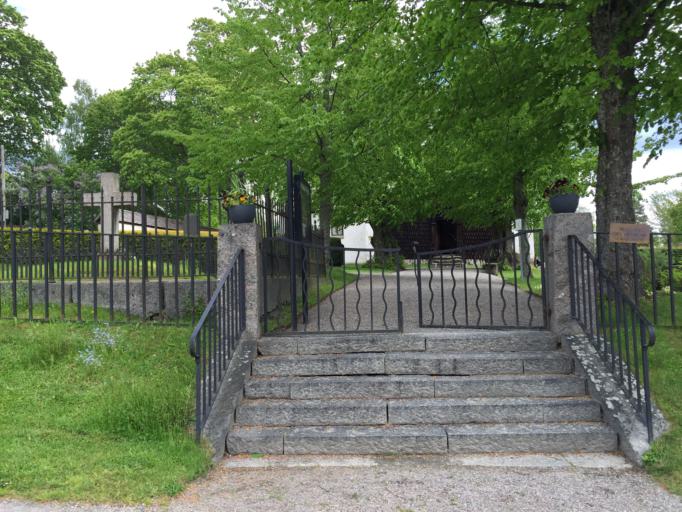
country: SE
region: OEstergoetland
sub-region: Finspangs Kommun
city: Finspang
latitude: 58.6752
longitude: 15.8433
